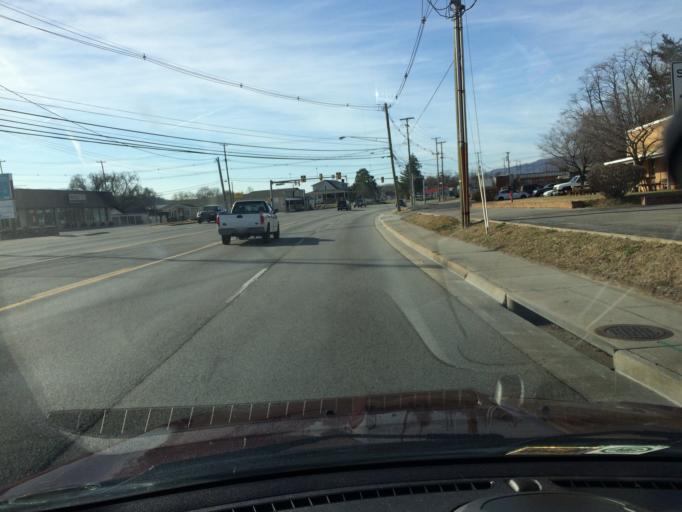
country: US
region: Virginia
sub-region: City of Salem
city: Salem
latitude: 37.2825
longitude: -80.1045
